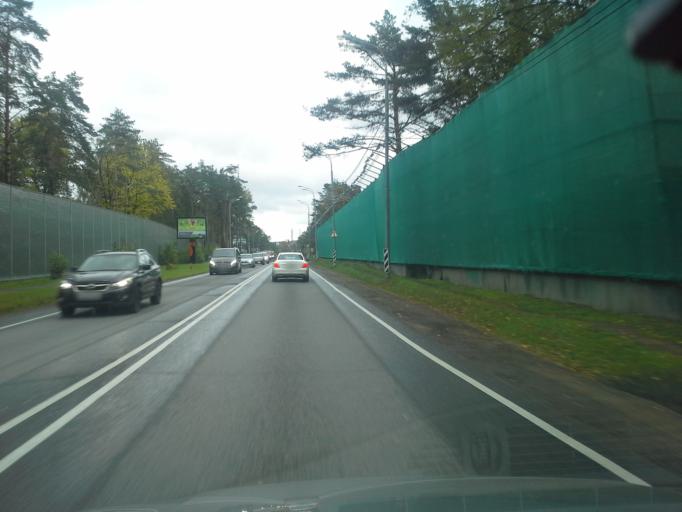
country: RU
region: Moskovskaya
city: Barvikha
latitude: 55.7443
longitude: 37.2900
